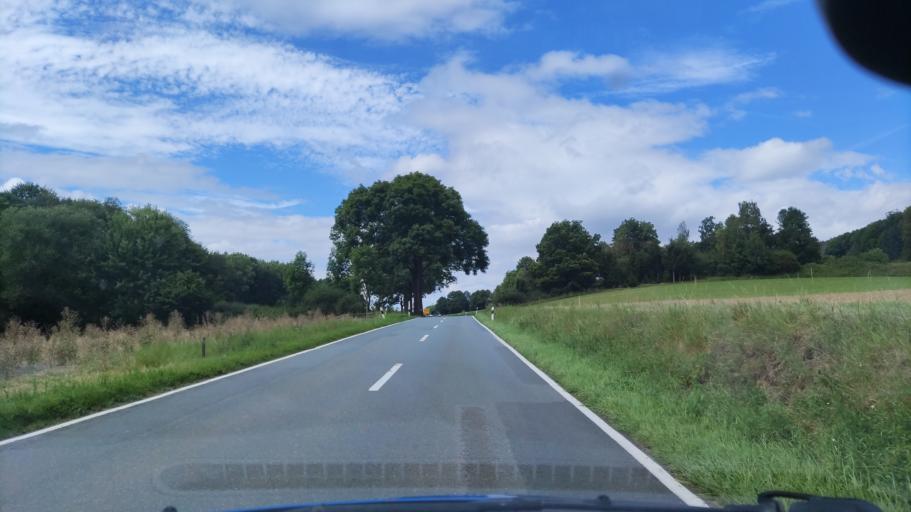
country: DE
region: Lower Saxony
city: Delligsen
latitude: 51.9584
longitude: 9.7836
